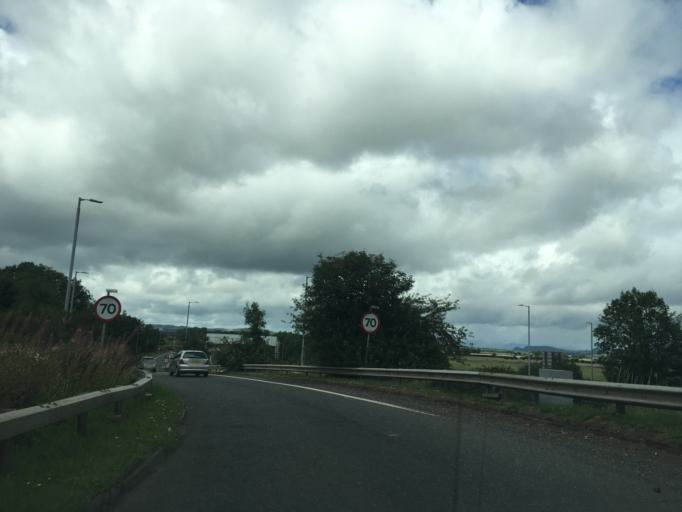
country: GB
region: Scotland
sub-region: Renfrewshire
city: Paisley
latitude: 55.8582
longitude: -4.4505
